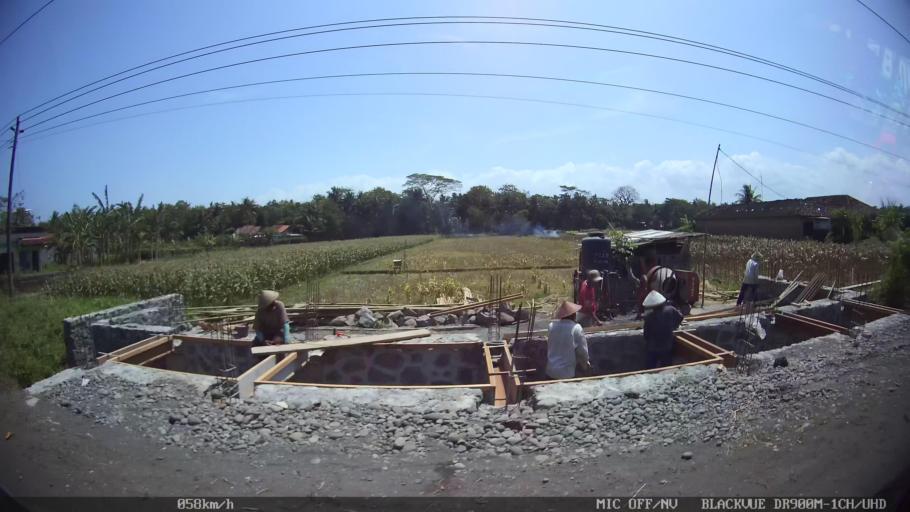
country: ID
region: Daerah Istimewa Yogyakarta
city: Srandakan
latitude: -7.9514
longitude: 110.2098
